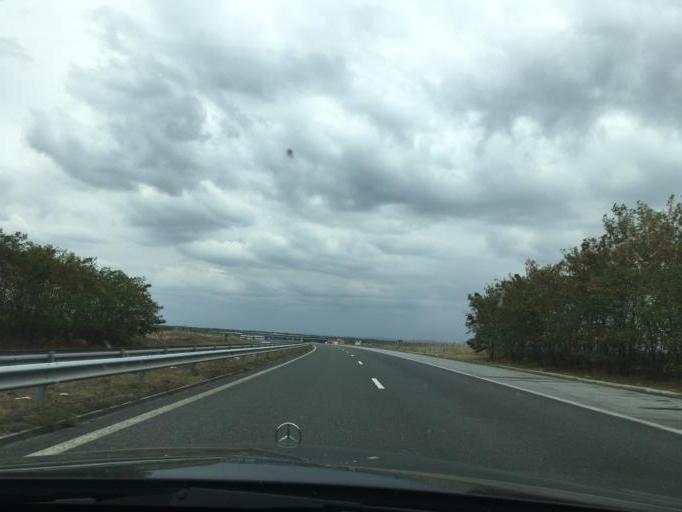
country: BG
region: Yambol
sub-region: Obshtina Yambol
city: Yambol
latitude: 42.5399
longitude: 26.4720
